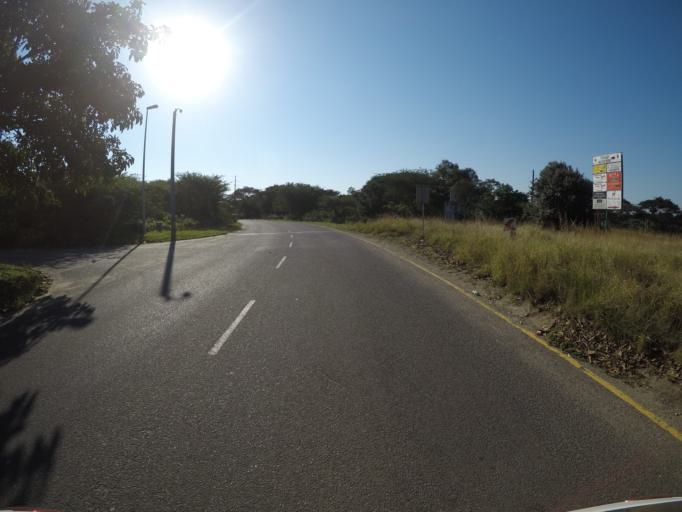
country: ZA
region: KwaZulu-Natal
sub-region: uThungulu District Municipality
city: Richards Bay
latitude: -28.7873
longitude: 32.0798
